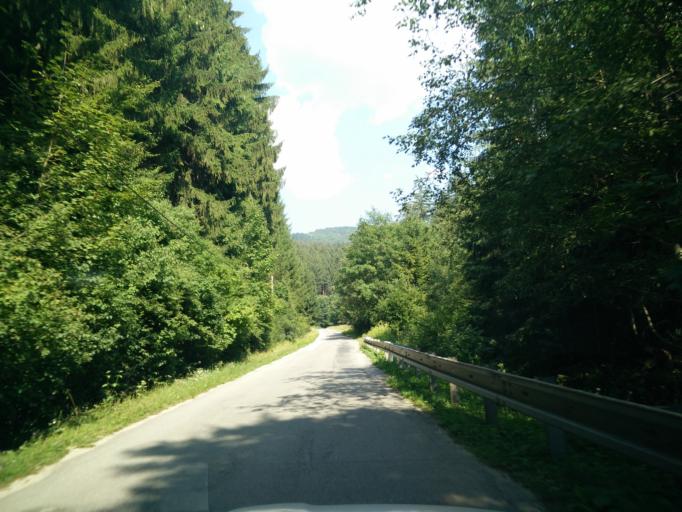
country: SK
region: Zilinsky
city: Rajec
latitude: 49.0922
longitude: 18.7207
